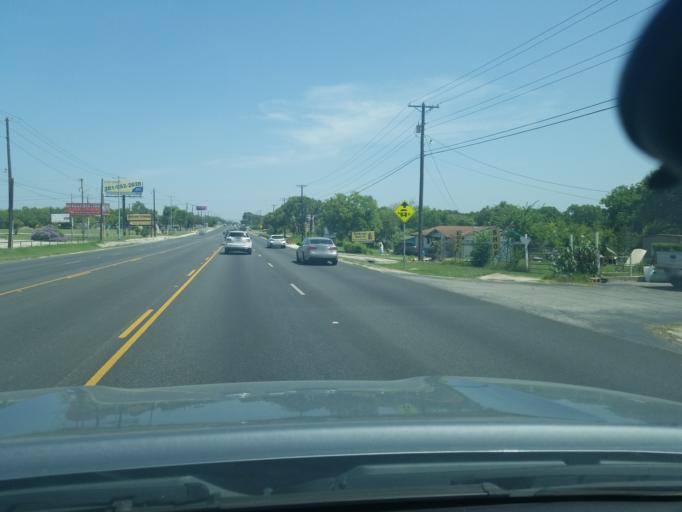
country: US
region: Texas
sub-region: Guadalupe County
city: Lake Dunlap
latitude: 29.6822
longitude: -98.0641
